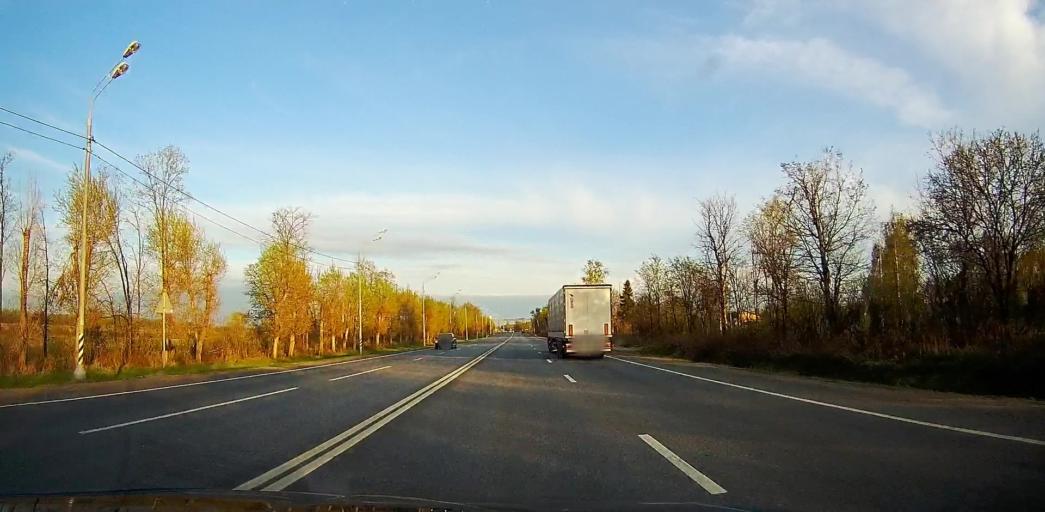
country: RU
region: Moskovskaya
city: Troitskoye
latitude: 55.2602
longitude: 38.5115
